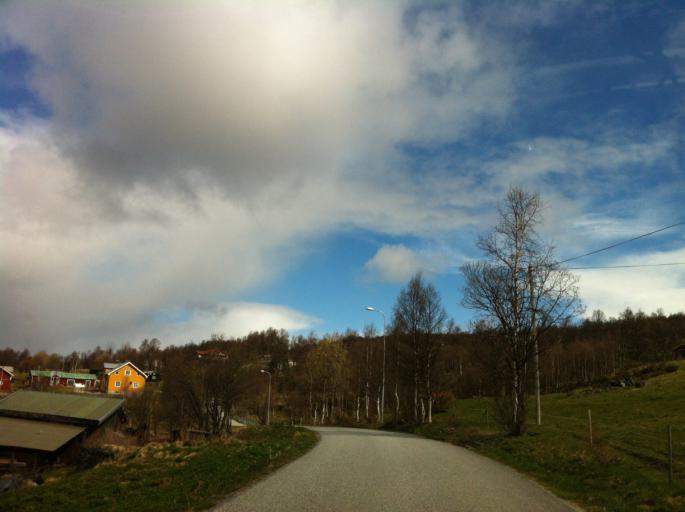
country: NO
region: Sor-Trondelag
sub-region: Tydal
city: Aas
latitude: 62.6346
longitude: 12.4450
